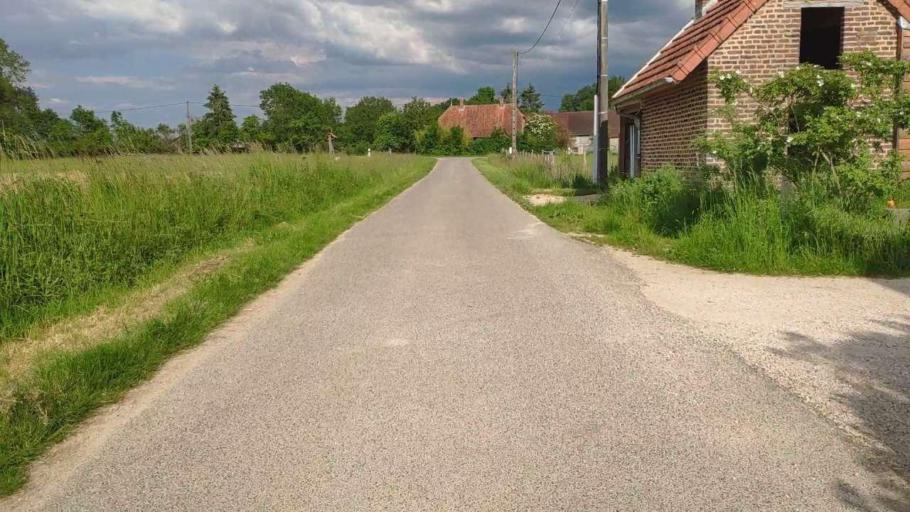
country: FR
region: Bourgogne
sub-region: Departement de Saone-et-Loire
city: Pierre-de-Bresse
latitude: 46.8190
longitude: 5.3406
